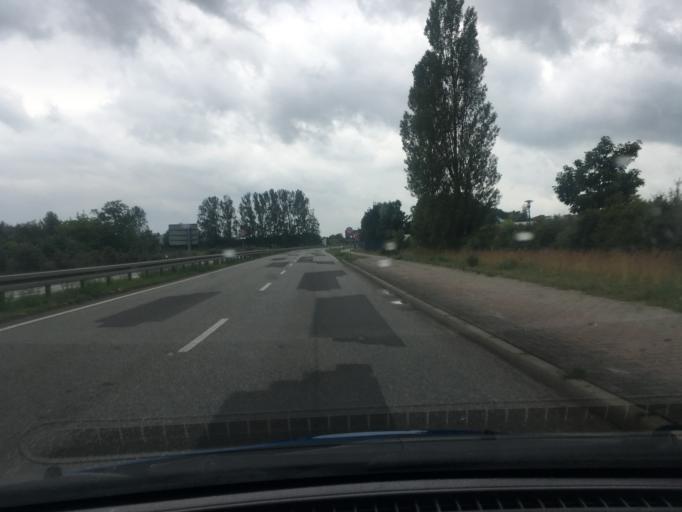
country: DE
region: Mecklenburg-Vorpommern
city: Klein Rogahn
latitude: 53.5710
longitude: 11.3878
